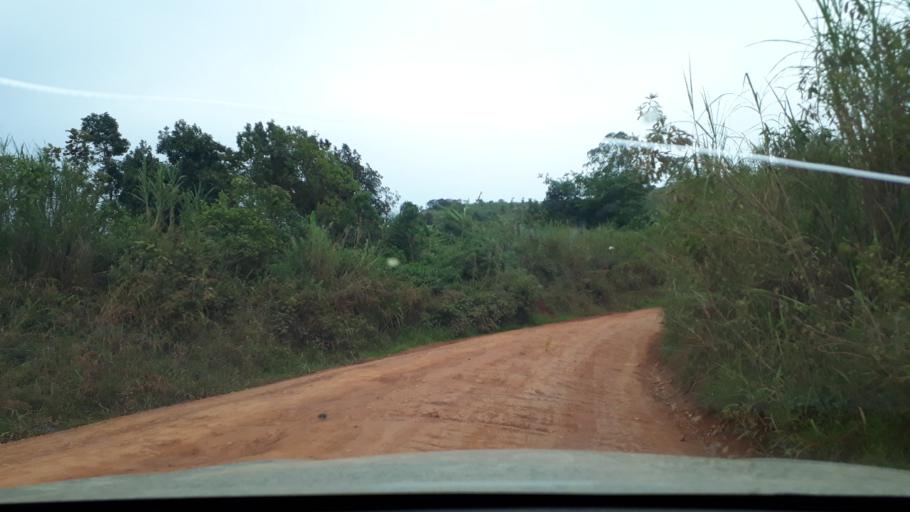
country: CD
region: Eastern Province
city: Bunia
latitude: 1.8014
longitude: 30.3870
